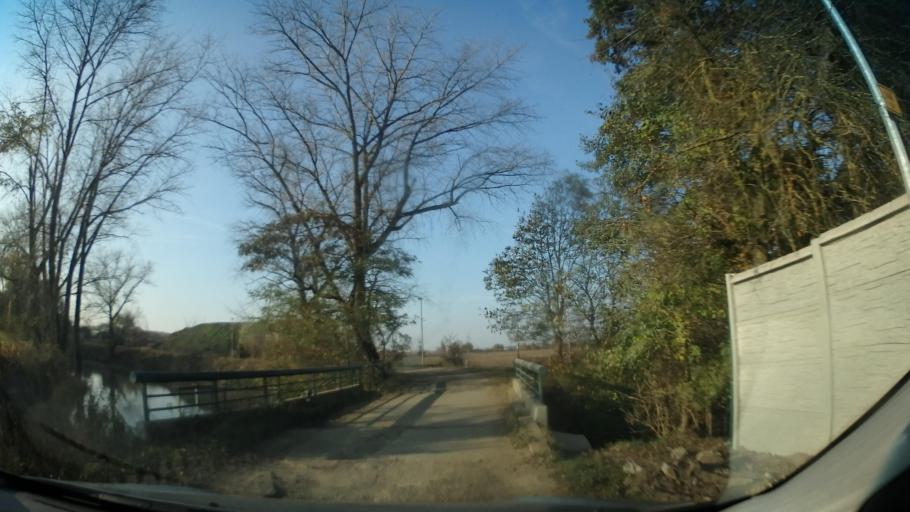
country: CZ
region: Praha
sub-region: Praha 20
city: Horni Pocernice
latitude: 50.0782
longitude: 14.6186
